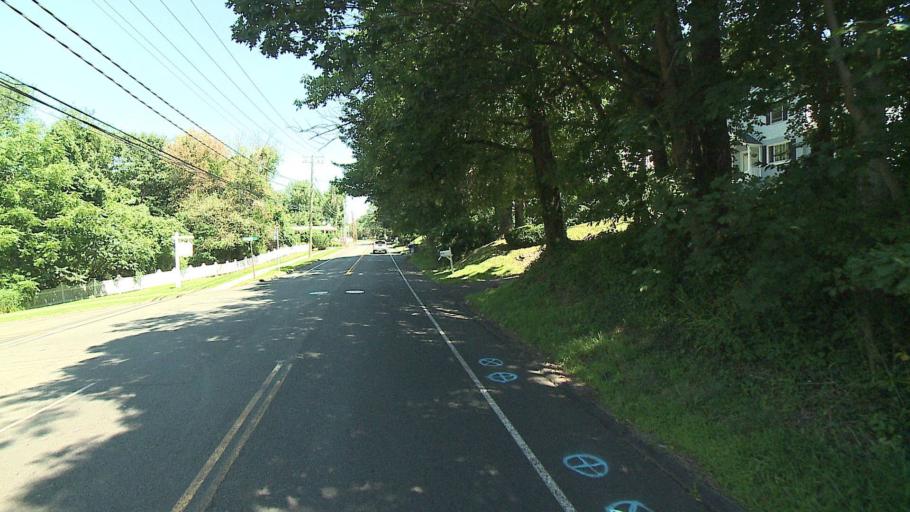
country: US
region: Connecticut
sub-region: Fairfield County
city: Trumbull
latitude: 41.2525
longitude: -73.2198
